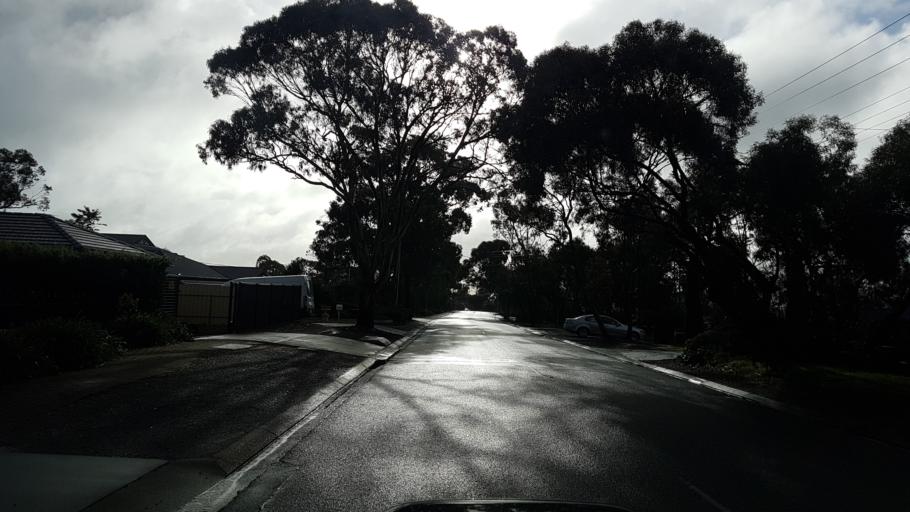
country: AU
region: South Australia
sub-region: Onkaparinga
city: Craigburn Farm
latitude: -35.0657
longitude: 138.6102
